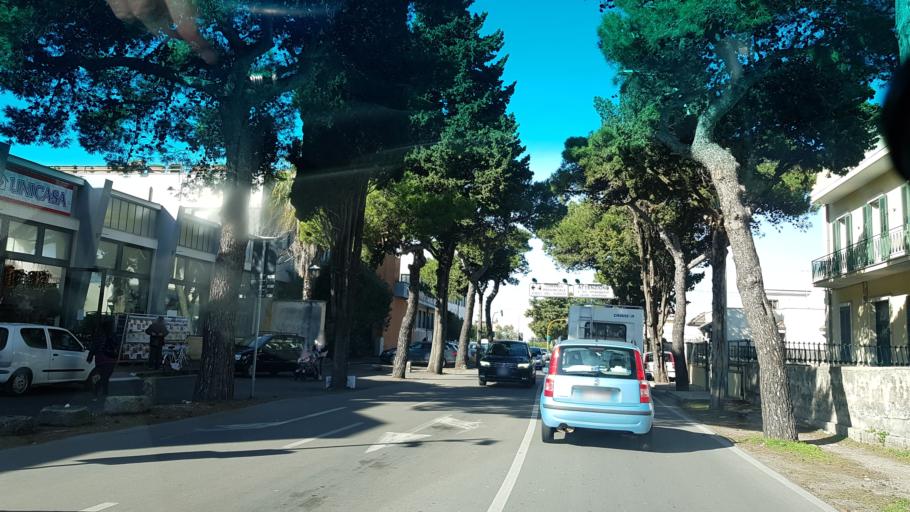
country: IT
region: Apulia
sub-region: Provincia di Lecce
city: Lecce
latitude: 40.3434
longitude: 18.1589
